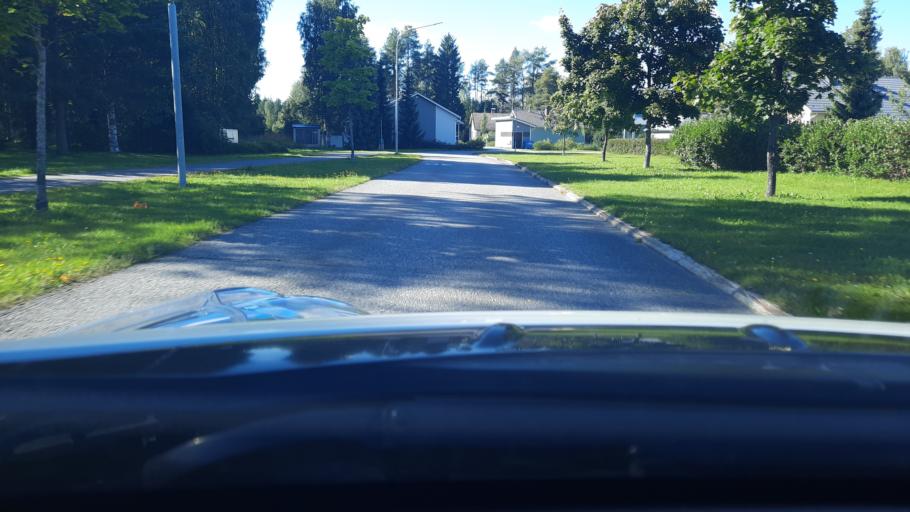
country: FI
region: North Karelia
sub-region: Joensuu
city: Joensuu
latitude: 62.6350
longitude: 29.6854
